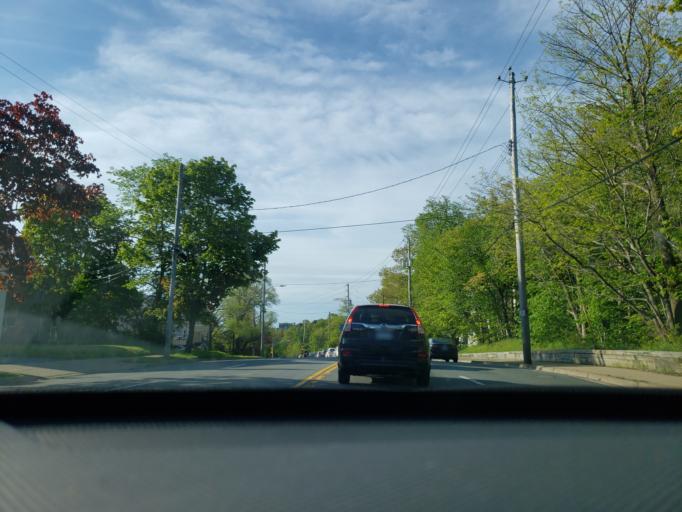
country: CA
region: Nova Scotia
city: Dartmouth
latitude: 44.6498
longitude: -63.6306
